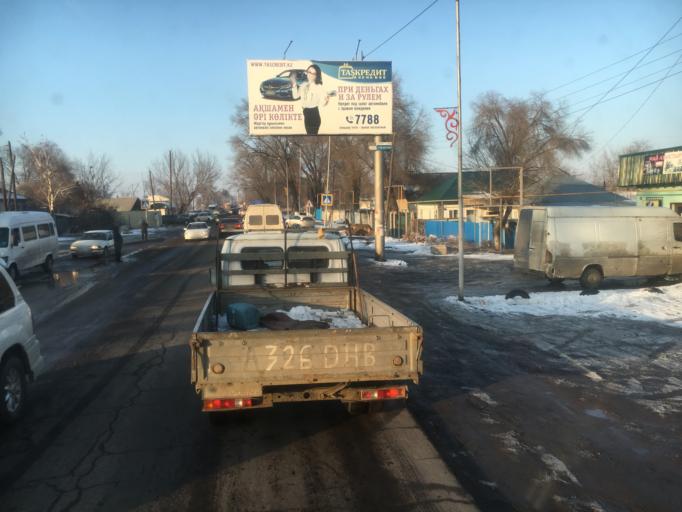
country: KZ
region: Almaty Oblysy
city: Burunday
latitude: 43.3749
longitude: 76.6419
